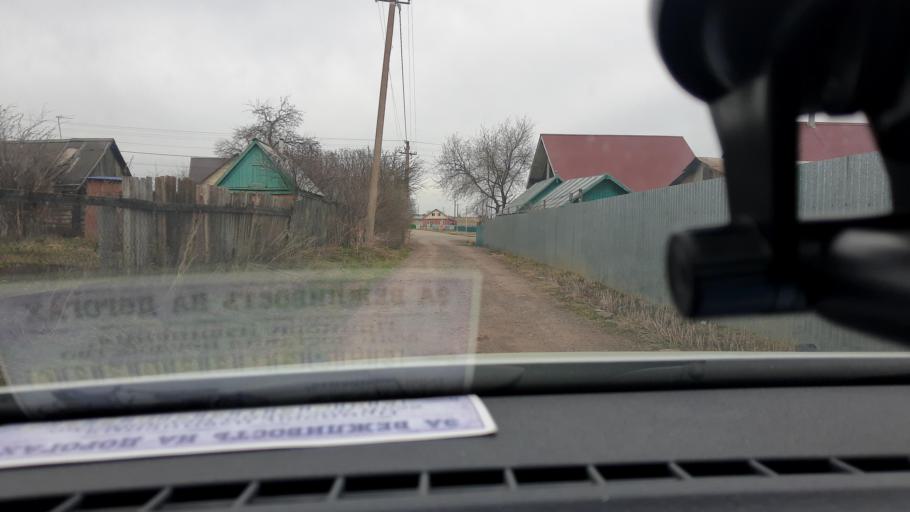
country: RU
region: Bashkortostan
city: Avdon
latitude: 54.5697
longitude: 55.5843
